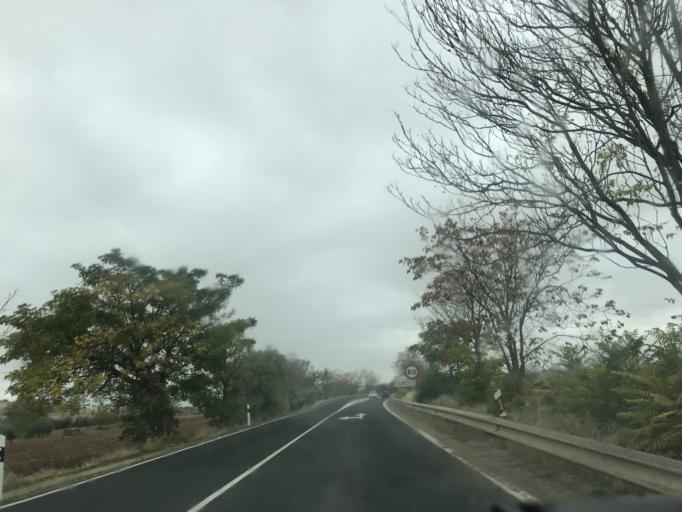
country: ES
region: Andalusia
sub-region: Provincia de Jaen
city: Peal de Becerro
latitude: 37.9141
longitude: -3.1018
